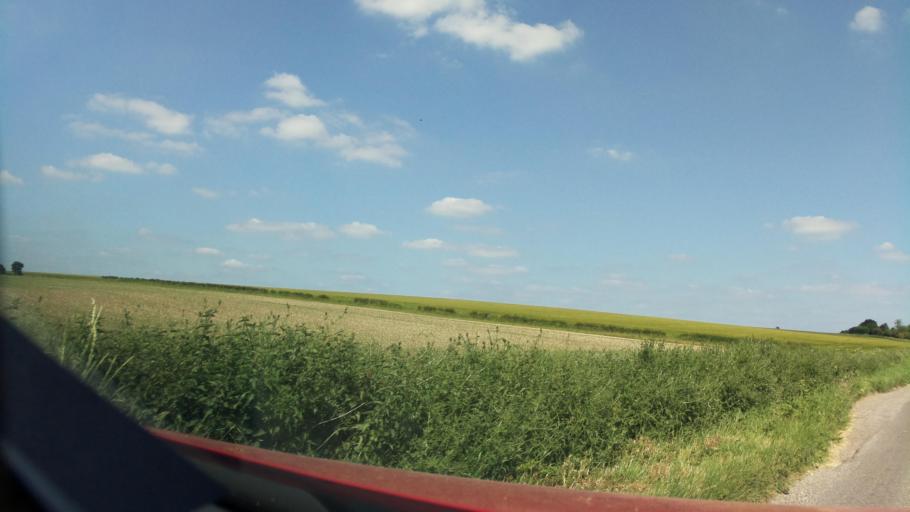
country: GB
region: England
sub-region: Wiltshire
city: Collingbourne Kingston
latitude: 51.2833
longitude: -1.6645
